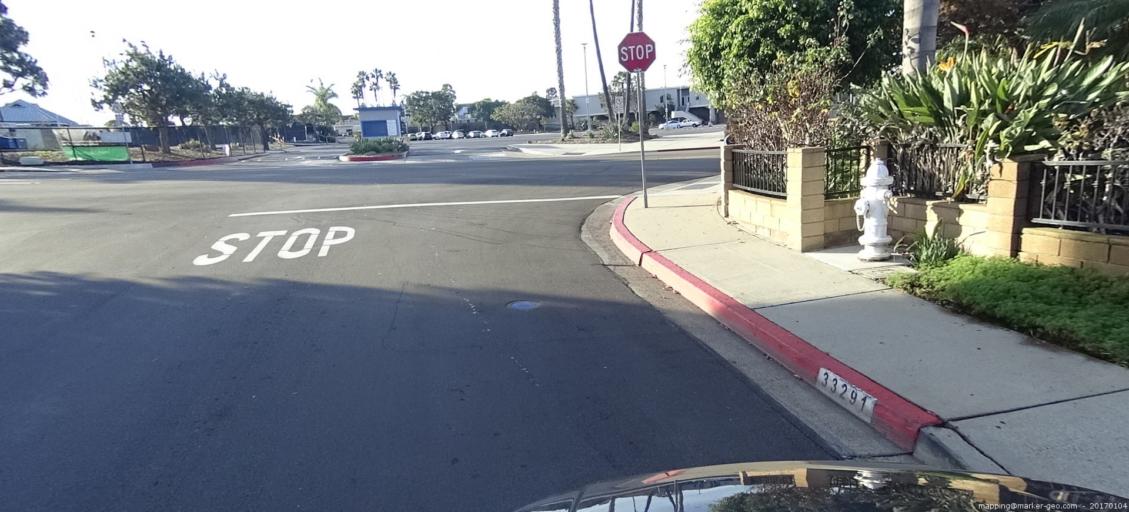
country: US
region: California
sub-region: Orange County
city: Dana Point
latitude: 33.4795
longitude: -117.6993
